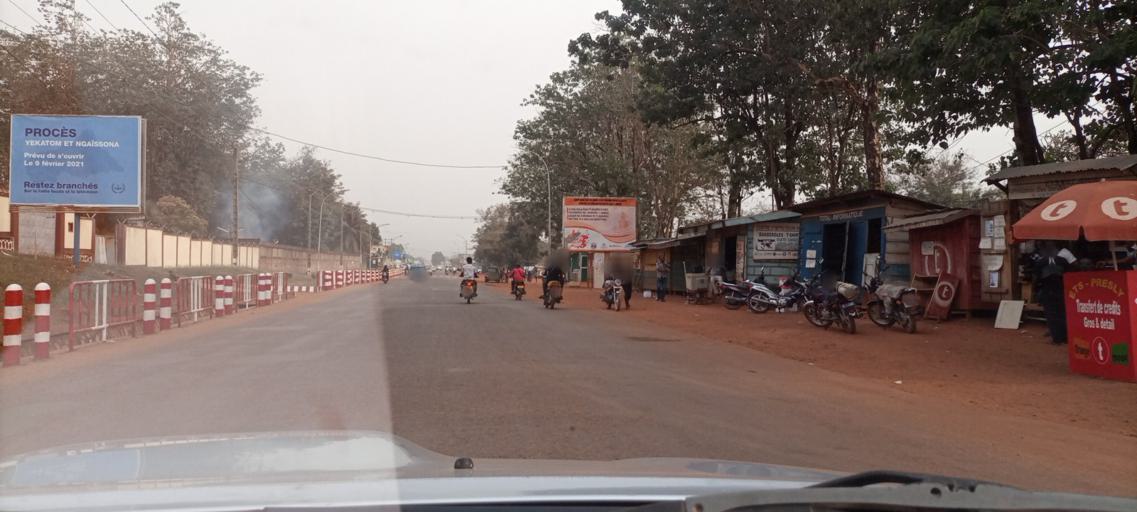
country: CF
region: Bangui
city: Bangui
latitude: 4.3739
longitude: 18.5719
